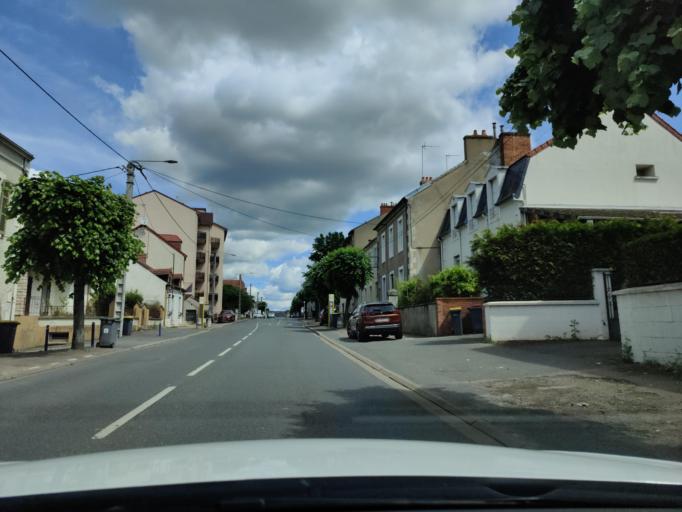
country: FR
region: Auvergne
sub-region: Departement de l'Allier
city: Montlucon
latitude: 46.3317
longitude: 2.6089
